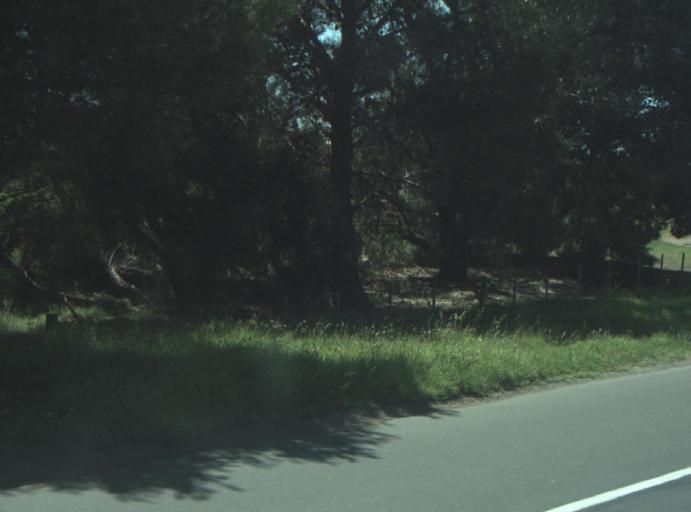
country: AU
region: Victoria
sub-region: Greater Geelong
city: Breakwater
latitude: -38.1867
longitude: 144.3549
